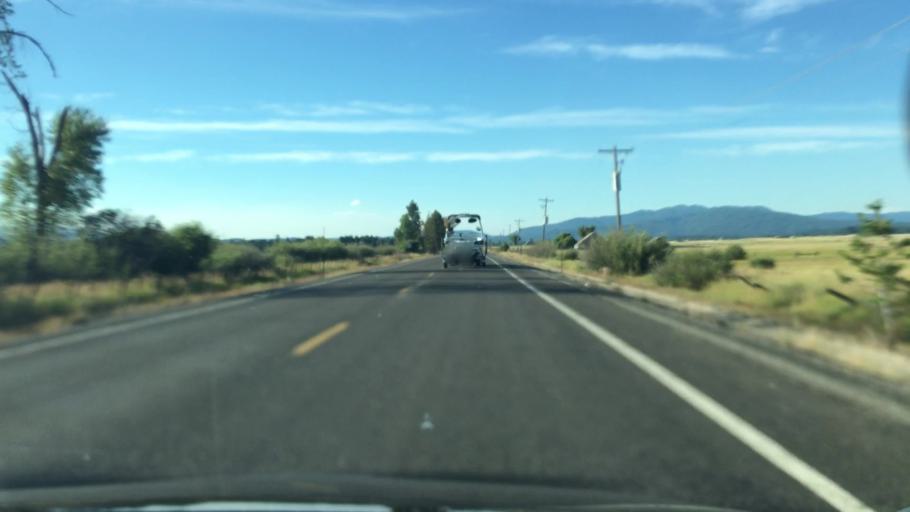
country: US
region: Idaho
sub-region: Valley County
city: Cascade
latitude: 44.4276
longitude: -115.9995
